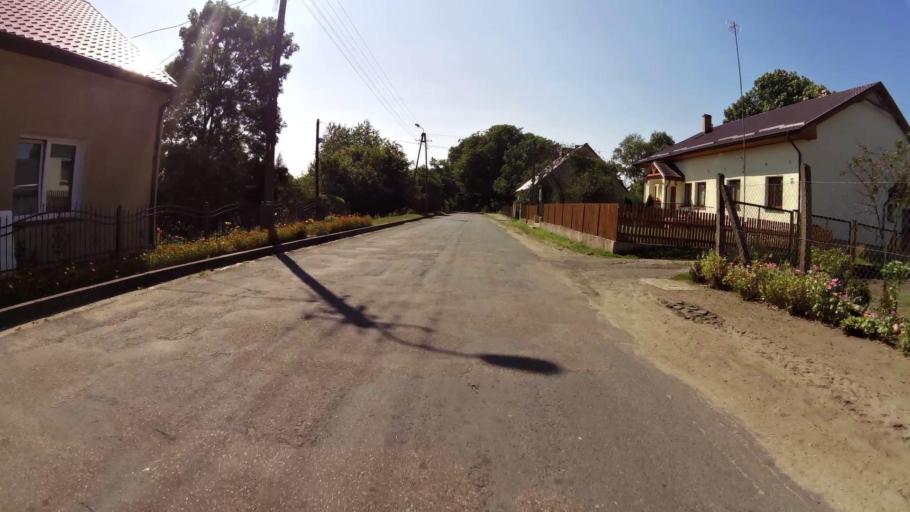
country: PL
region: West Pomeranian Voivodeship
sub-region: Powiat drawski
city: Czaplinek
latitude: 53.4428
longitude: 16.2703
